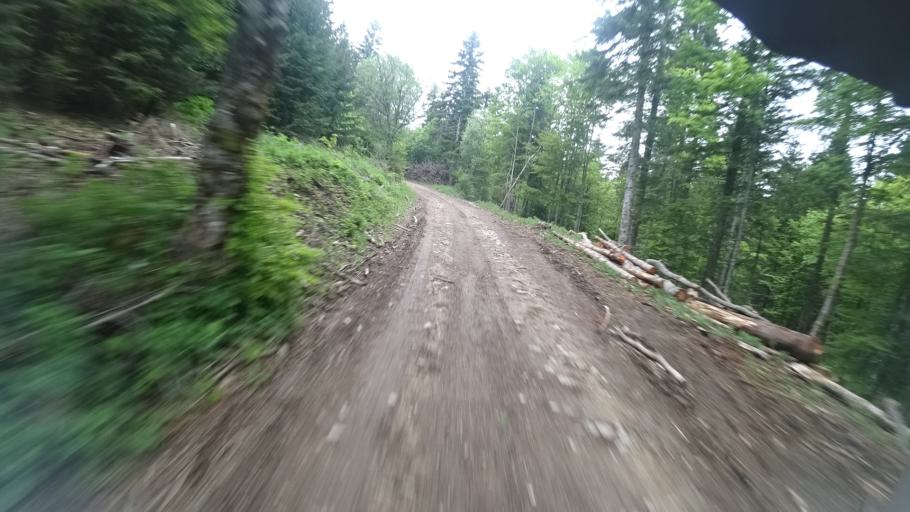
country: BA
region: Federation of Bosnia and Herzegovina
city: Bihac
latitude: 44.6386
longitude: 15.8211
